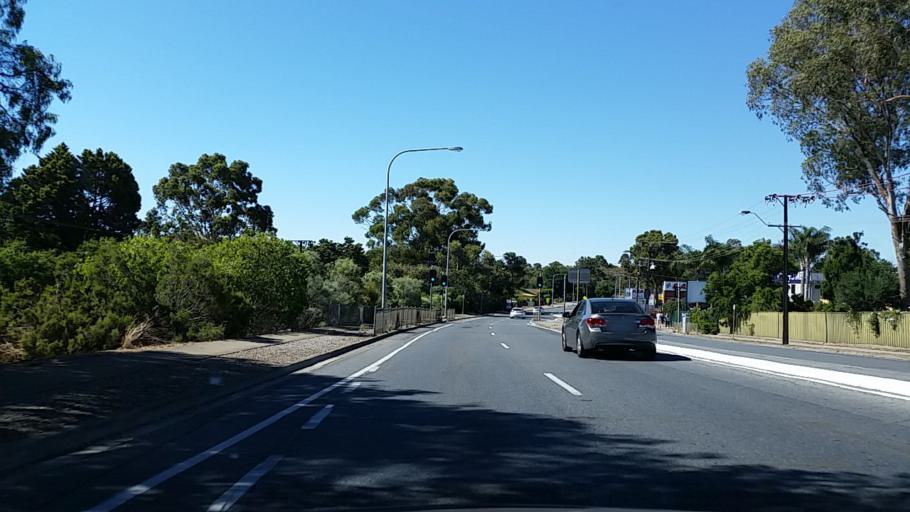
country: AU
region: South Australia
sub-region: Tea Tree Gully
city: Hope Valley
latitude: -34.8266
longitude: 138.6936
